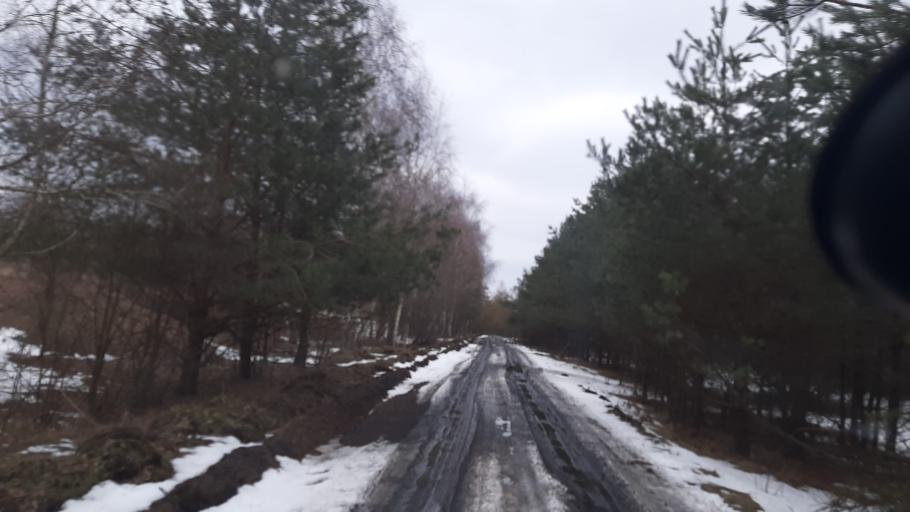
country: PL
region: Lublin Voivodeship
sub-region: Powiat wlodawski
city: Wlodawa
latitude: 51.5145
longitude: 23.6081
